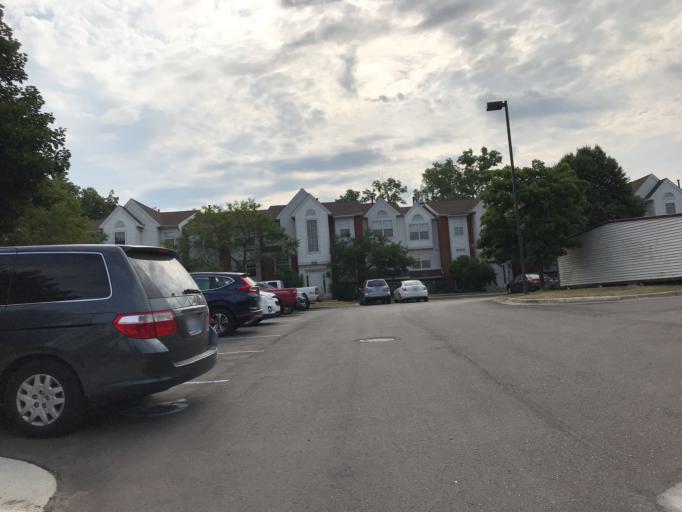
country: US
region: Michigan
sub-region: Washtenaw County
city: Ann Arbor
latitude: 42.2514
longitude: -83.7221
